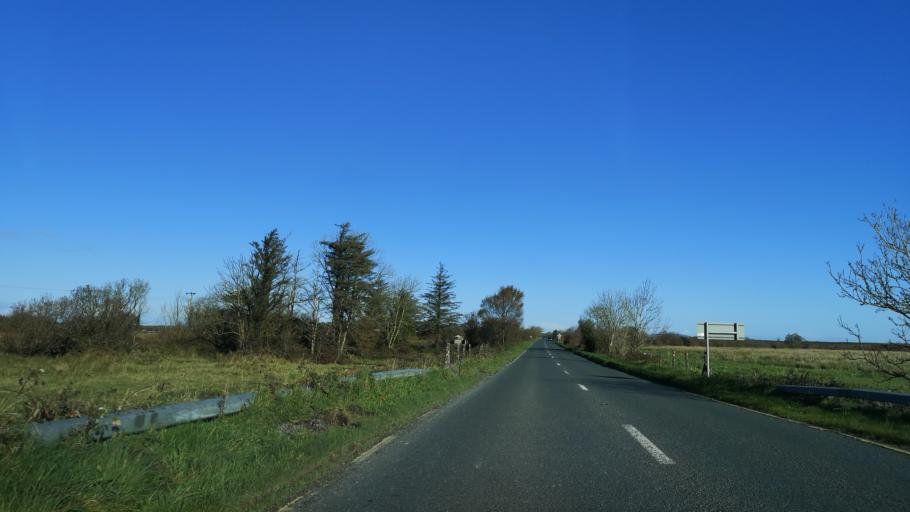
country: IE
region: Connaught
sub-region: County Galway
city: Claregalway
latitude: 53.3420
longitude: -9.0193
